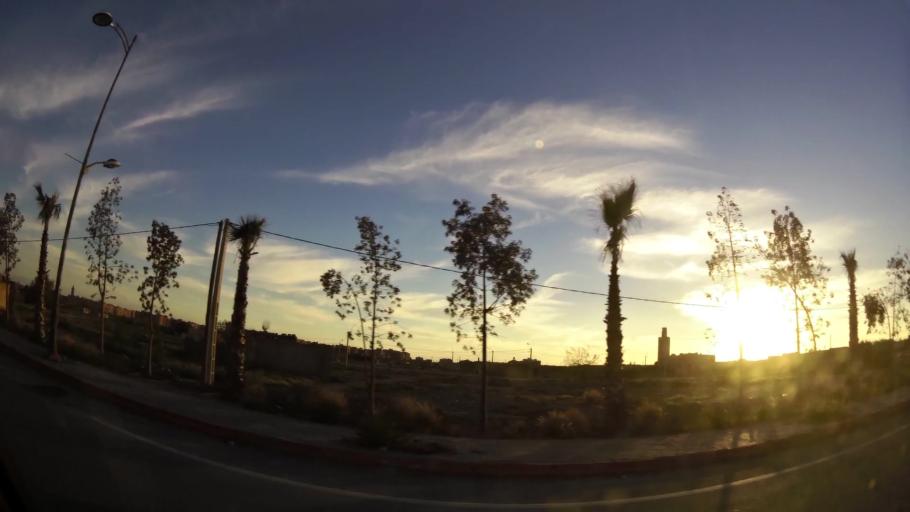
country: MA
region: Marrakech-Tensift-Al Haouz
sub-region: Marrakech
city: Marrakesh
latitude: 31.7580
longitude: -8.1134
